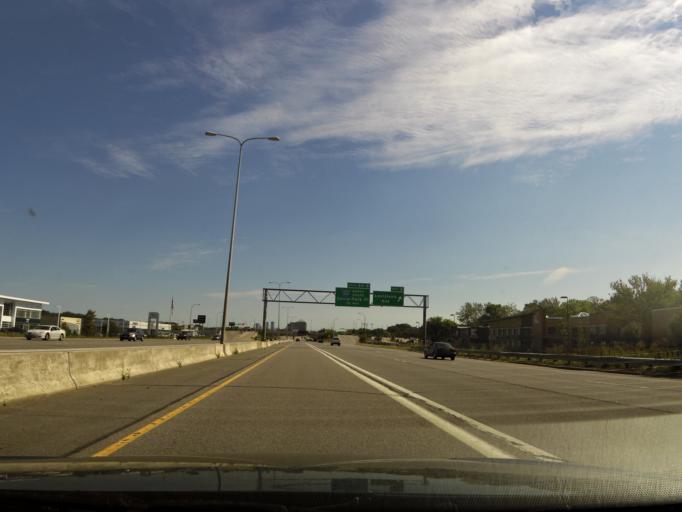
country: US
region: Minnesota
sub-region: Hennepin County
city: Saint Louis Park
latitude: 44.9713
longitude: -93.3763
